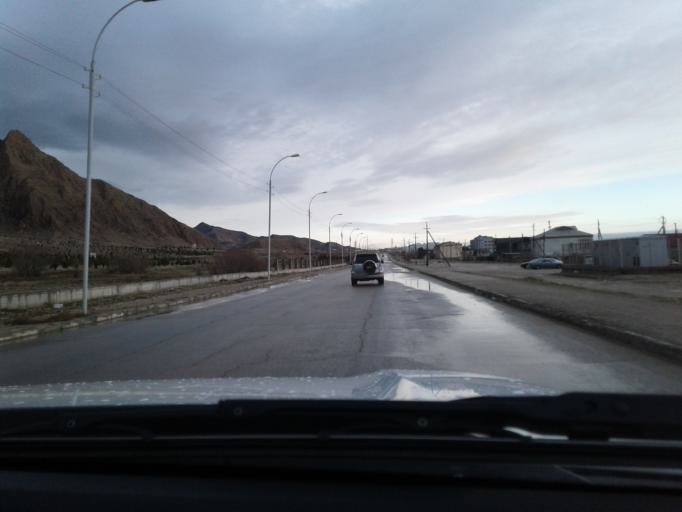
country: TM
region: Balkan
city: Balkanabat
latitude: 39.5293
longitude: 54.3585
